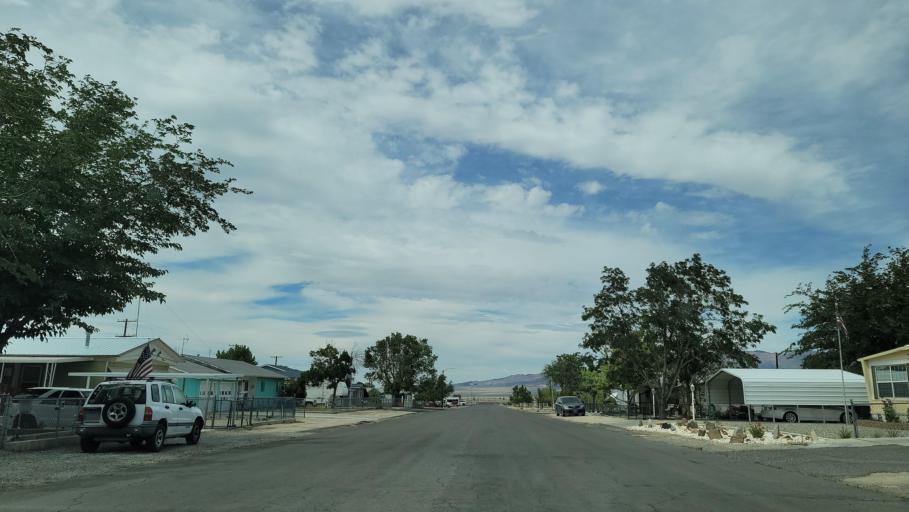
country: US
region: Nevada
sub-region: Mineral County
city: Hawthorne
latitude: 38.5295
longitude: -118.6190
